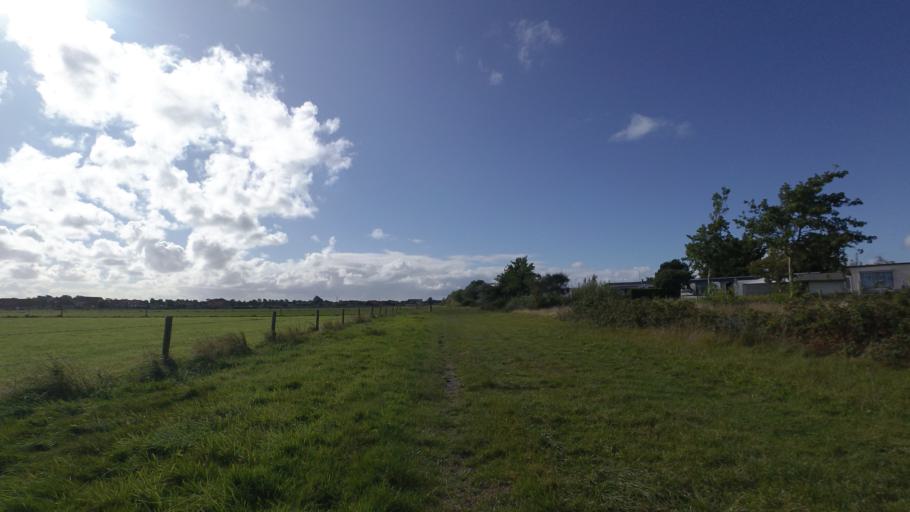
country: NL
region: Friesland
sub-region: Gemeente Ameland
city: Nes
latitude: 53.4513
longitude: 5.8101
